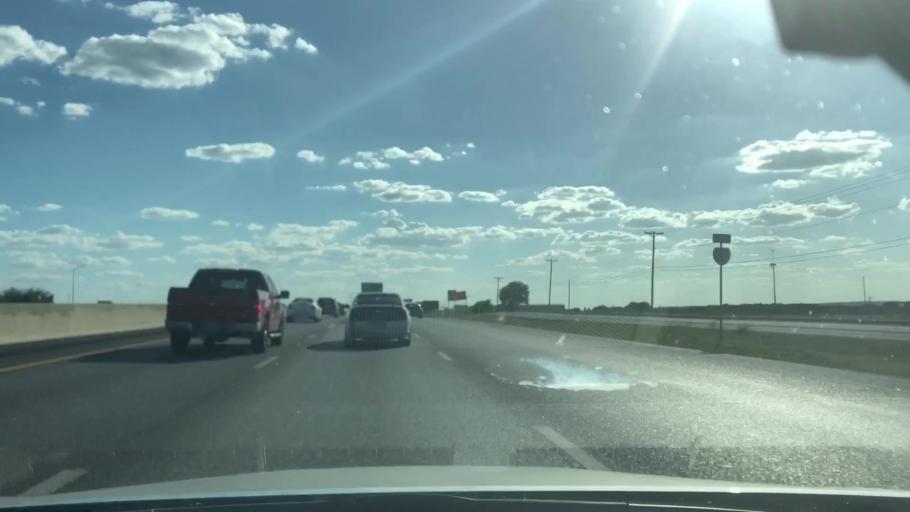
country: US
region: Texas
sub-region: Guadalupe County
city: Northcliff
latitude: 29.6370
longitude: -98.2158
